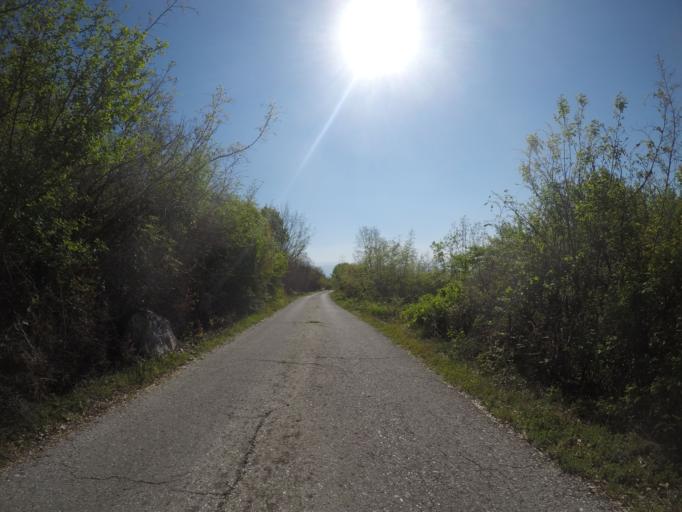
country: ME
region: Danilovgrad
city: Danilovgrad
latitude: 42.5168
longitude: 19.0614
